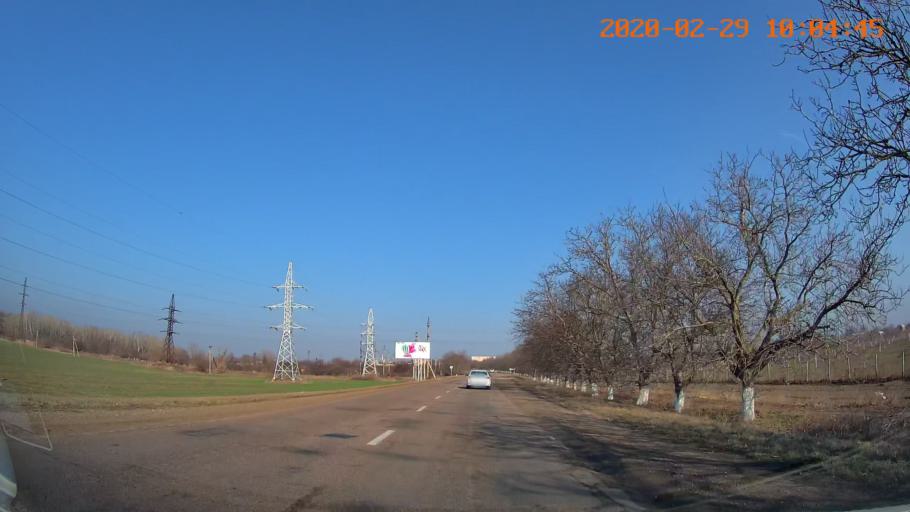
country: MD
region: Causeni
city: Chitcani
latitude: 46.8009
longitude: 29.6743
